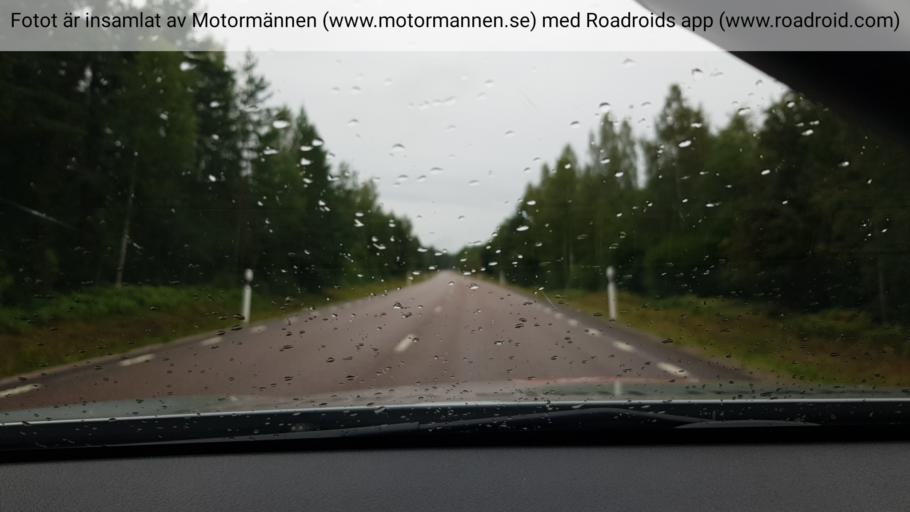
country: SE
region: Gaevleborg
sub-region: Gavle Kommun
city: Hedesunda
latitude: 60.3986
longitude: 16.9770
